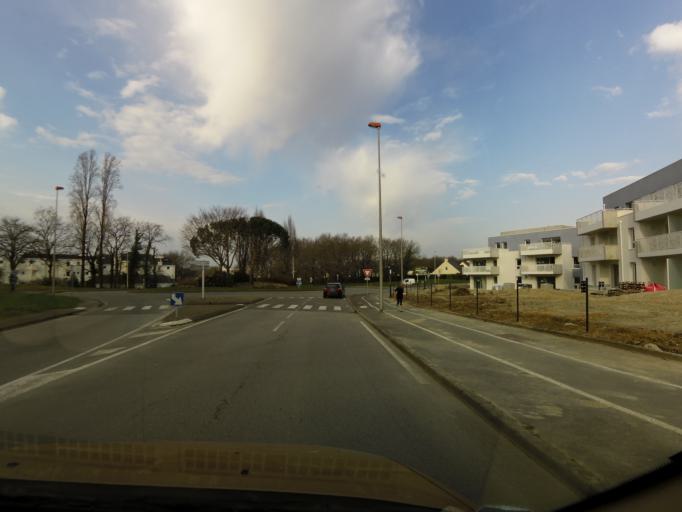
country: FR
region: Brittany
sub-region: Departement du Morbihan
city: Vannes
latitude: 47.6589
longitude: -2.7319
